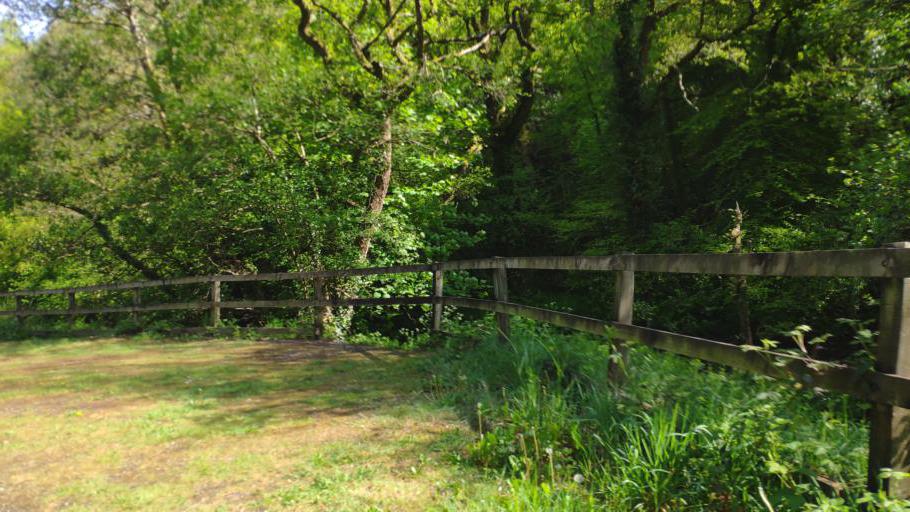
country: IE
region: Munster
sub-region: County Cork
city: Blarney
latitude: 51.9420
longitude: -8.5647
